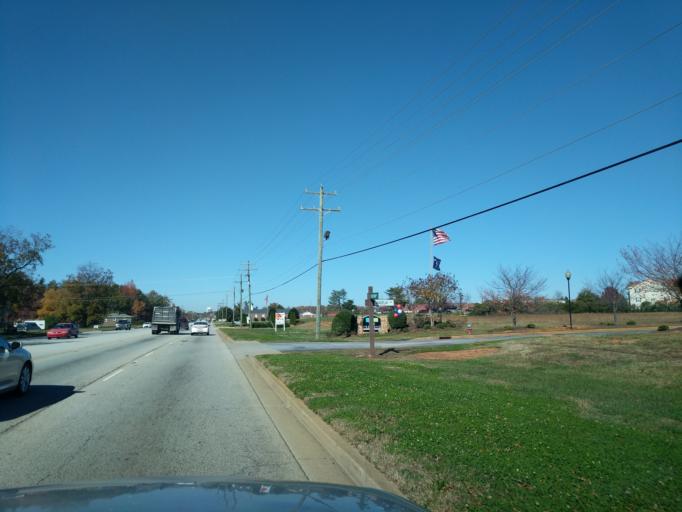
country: US
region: South Carolina
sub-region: Greenville County
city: Greer
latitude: 34.9308
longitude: -82.2496
